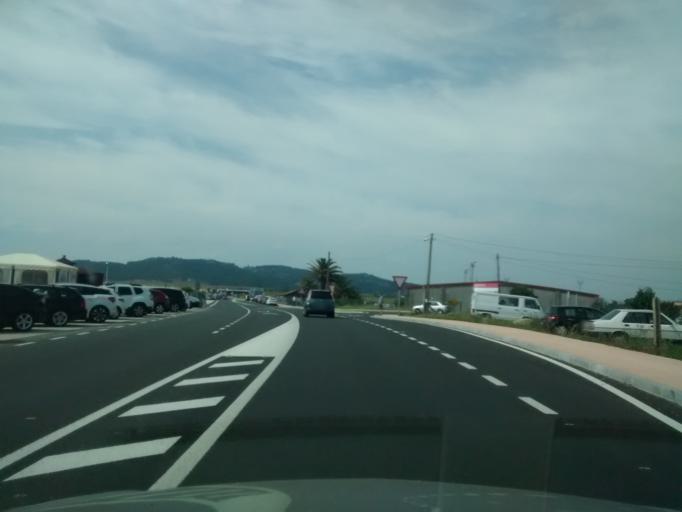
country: ES
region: Galicia
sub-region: Provincia de Pontevedra
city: O Grove
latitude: 42.4367
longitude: -8.8705
